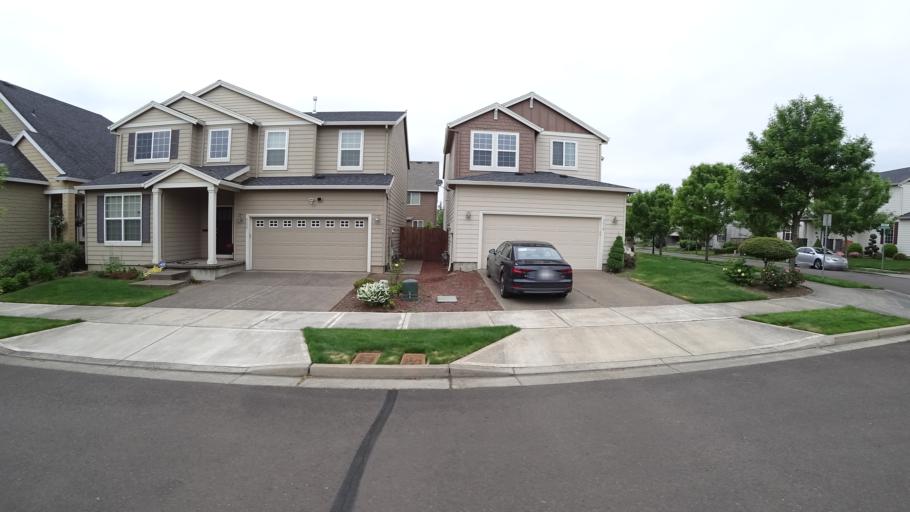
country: US
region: Oregon
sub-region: Washington County
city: Aloha
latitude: 45.4956
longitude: -122.9223
